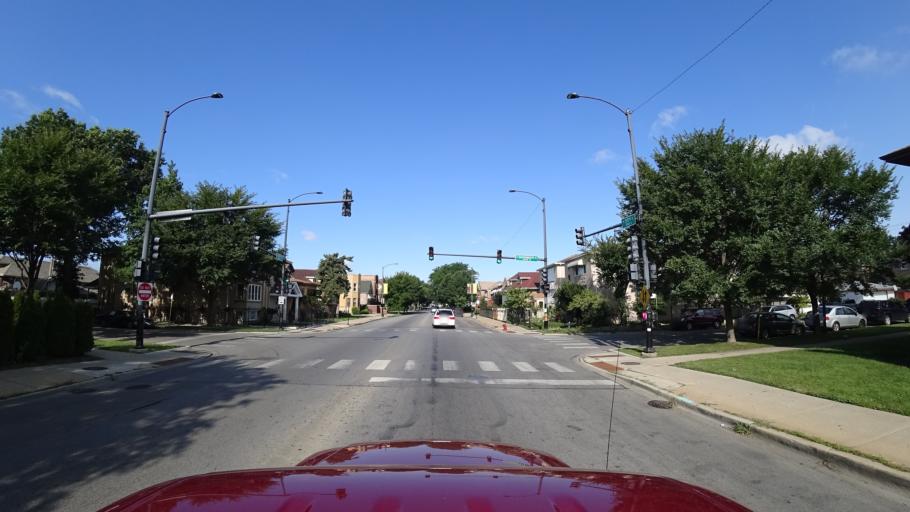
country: US
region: Illinois
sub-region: Cook County
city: Hometown
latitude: 41.7936
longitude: -87.6983
